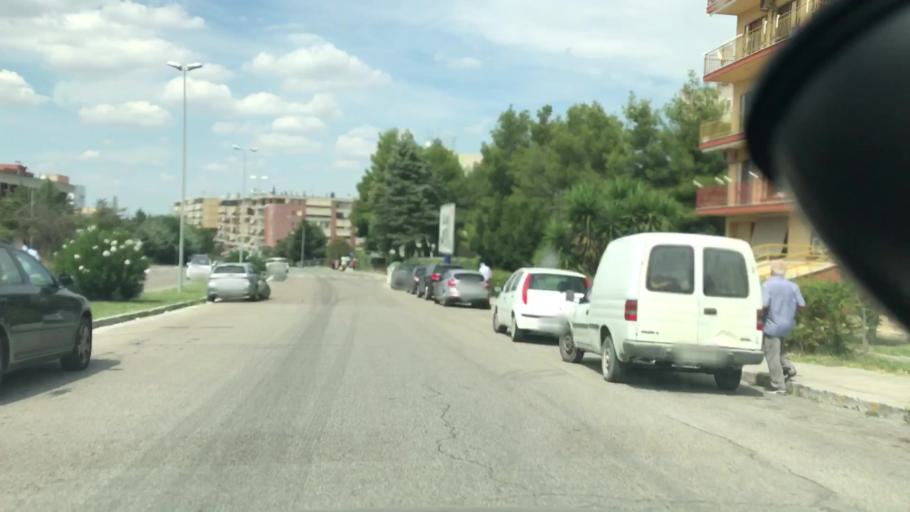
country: IT
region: Basilicate
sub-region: Provincia di Matera
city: Matera
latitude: 40.6756
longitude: 16.5837
